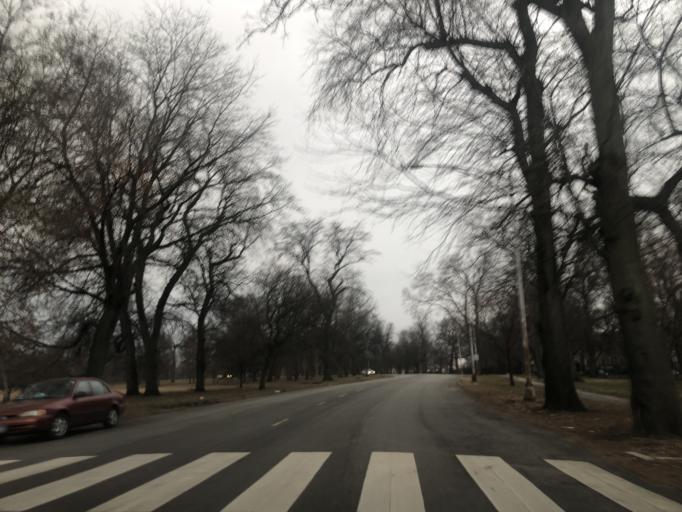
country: US
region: Illinois
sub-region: Cook County
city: Chicago
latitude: 41.7888
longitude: -87.6150
